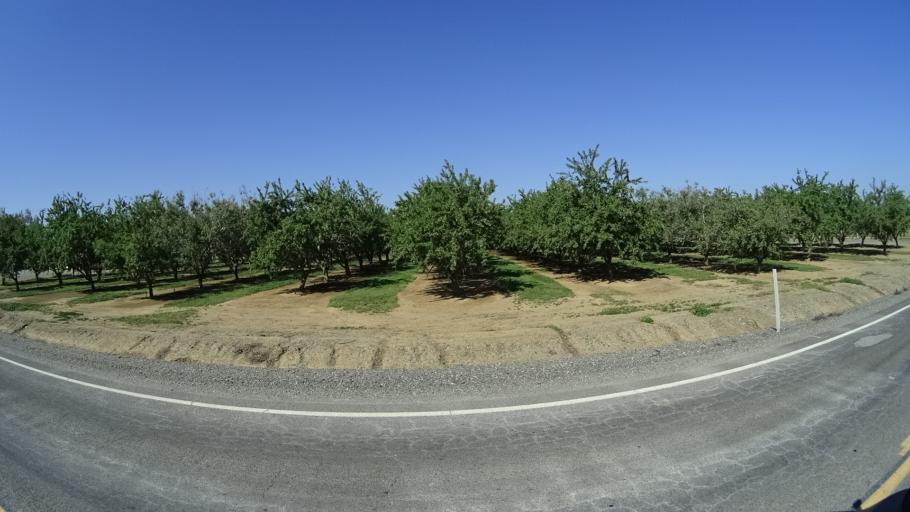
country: US
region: California
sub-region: Glenn County
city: Hamilton City
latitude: 39.6446
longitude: -122.0076
